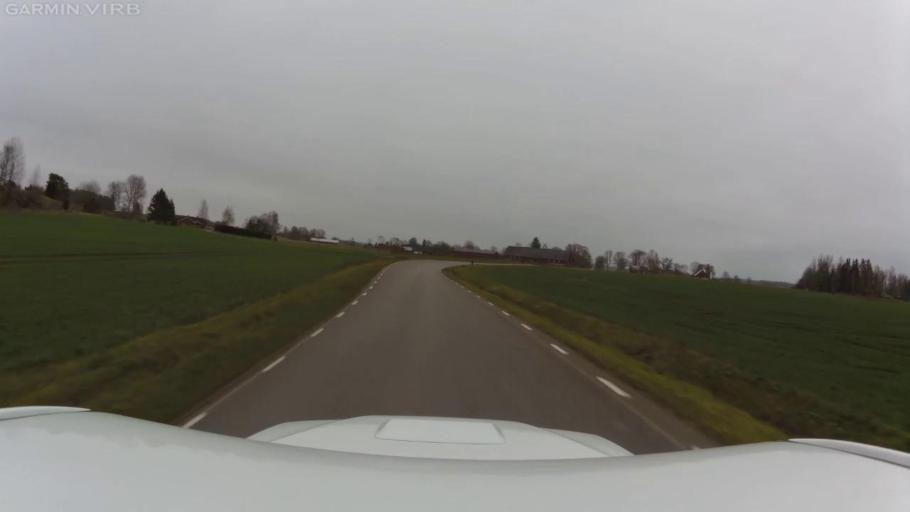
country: SE
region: OEstergoetland
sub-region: Linkopings Kommun
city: Vikingstad
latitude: 58.3115
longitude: 15.3784
